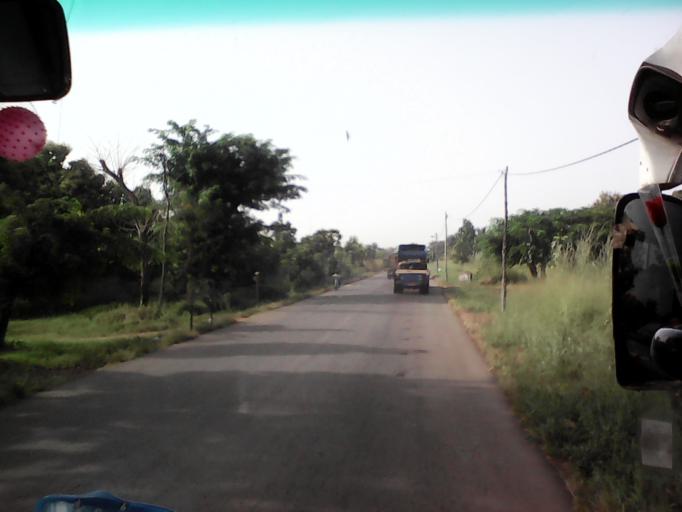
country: TG
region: Kara
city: Kara
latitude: 9.4575
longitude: 1.2155
